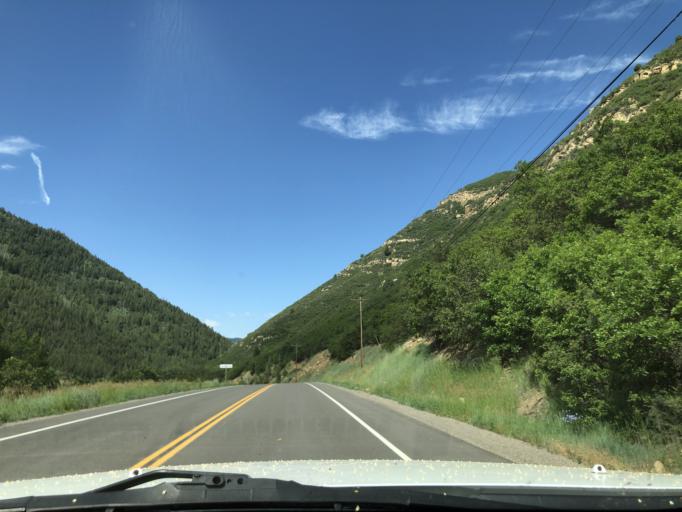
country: US
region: Colorado
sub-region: Delta County
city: Paonia
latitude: 38.9411
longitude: -107.3655
